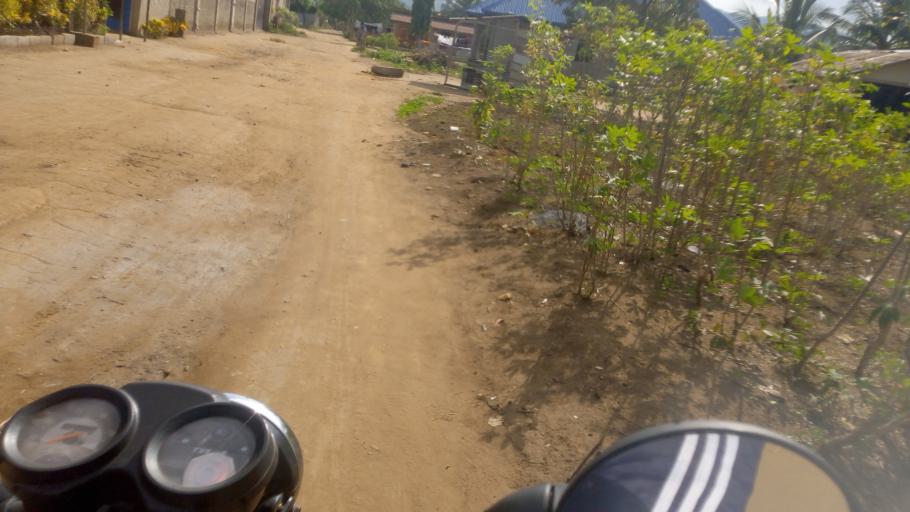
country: SL
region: Western Area
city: Waterloo
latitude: 8.3224
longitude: -13.0744
